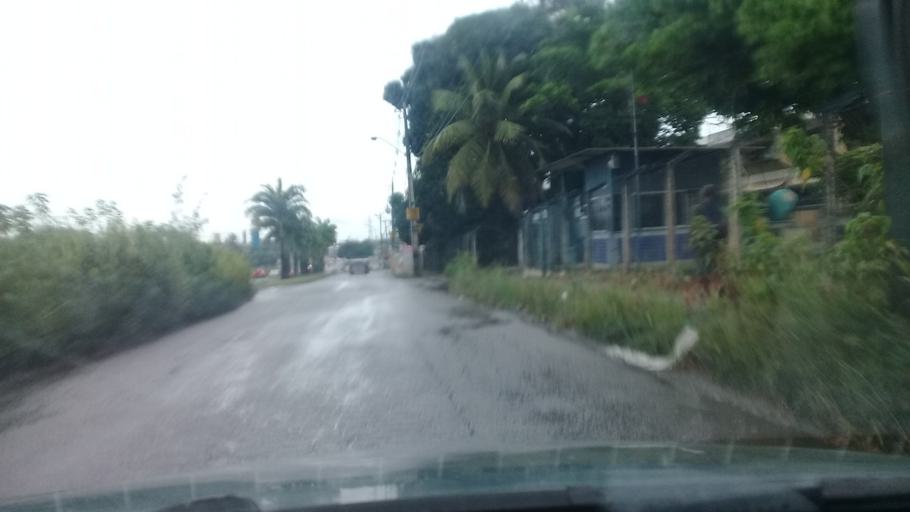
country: BR
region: Pernambuco
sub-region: Jaboatao Dos Guararapes
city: Jaboatao dos Guararapes
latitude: -8.0793
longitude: -34.9861
